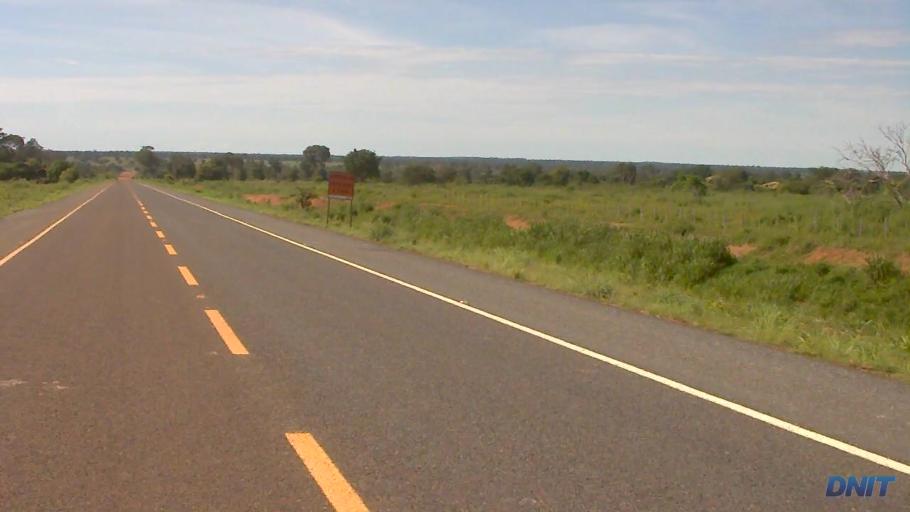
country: BR
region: Goias
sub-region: Sao Miguel Do Araguaia
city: Sao Miguel do Araguaia
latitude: -13.4897
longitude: -50.1094
